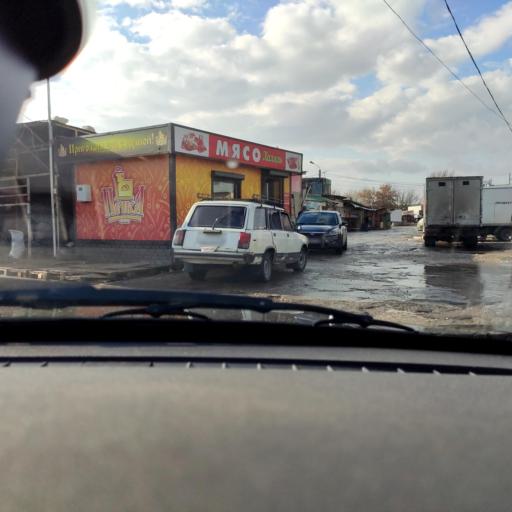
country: RU
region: Samara
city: Zhigulevsk
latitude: 53.5205
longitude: 49.4757
